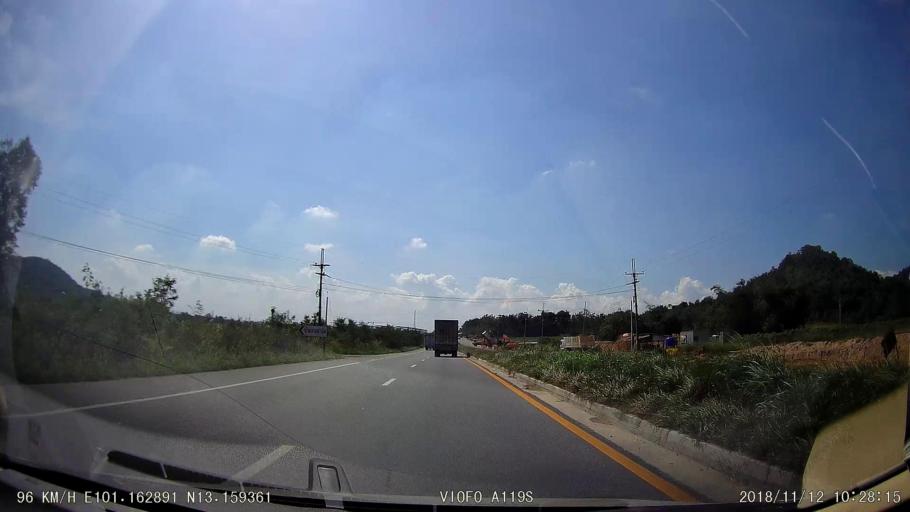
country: TH
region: Chon Buri
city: Ban Bueng
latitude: 13.1466
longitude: 101.1639
